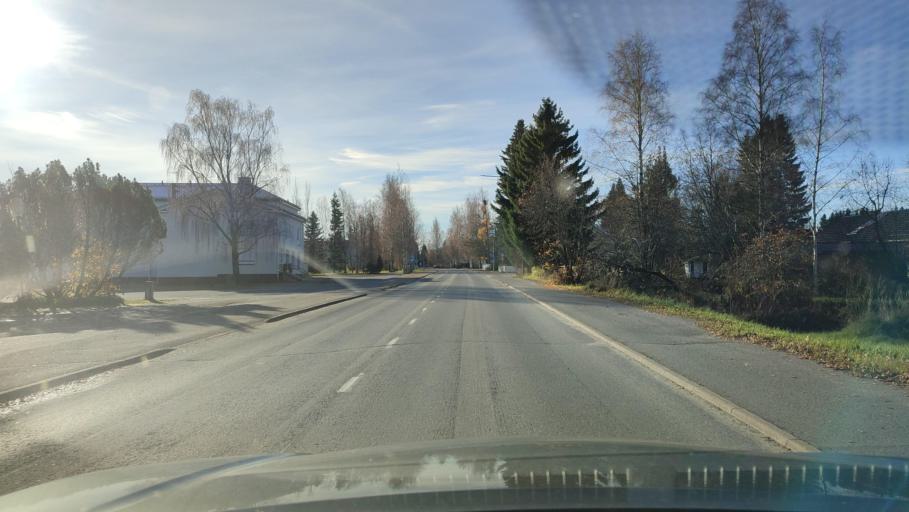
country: FI
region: Southern Ostrobothnia
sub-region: Suupohja
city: Teuva
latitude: 62.4847
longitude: 21.7455
